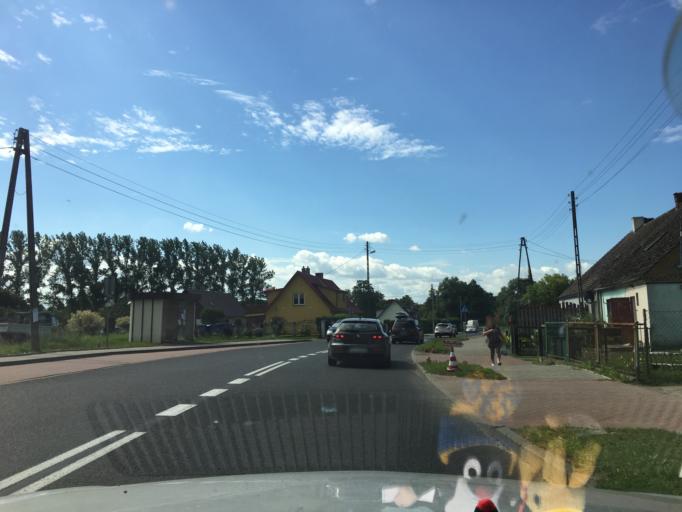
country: PL
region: West Pomeranian Voivodeship
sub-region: Powiat kamienski
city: Kamien Pomorski
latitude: 53.8888
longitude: 14.7907
